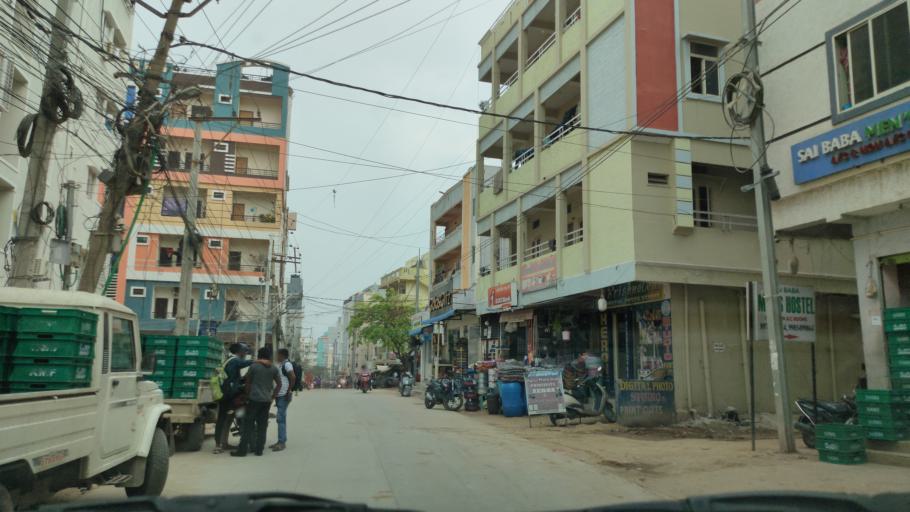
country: IN
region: Telangana
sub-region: Rangareddi
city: Kukatpalli
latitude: 17.4520
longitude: 78.3652
